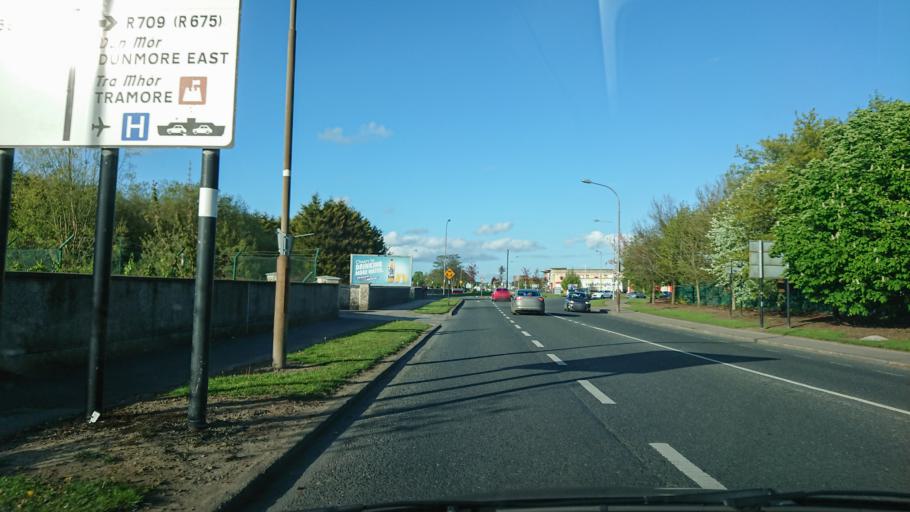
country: IE
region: Munster
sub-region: Waterford
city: Waterford
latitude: 52.2469
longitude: -7.1263
